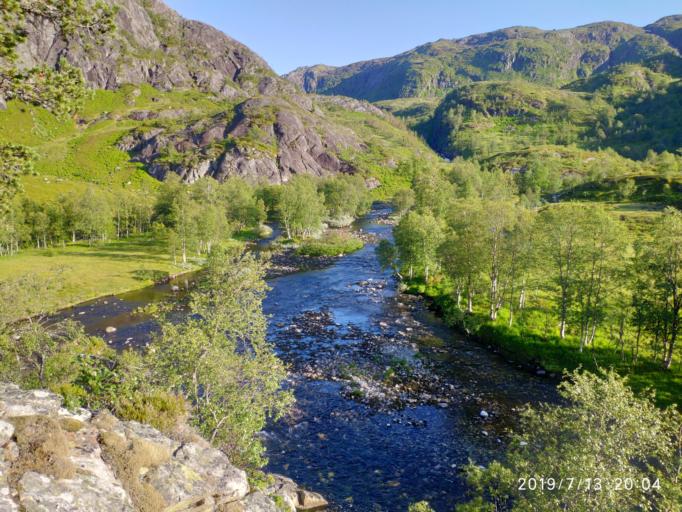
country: NO
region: Rogaland
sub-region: Sauda
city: Sauda
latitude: 59.8394
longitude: 6.3473
